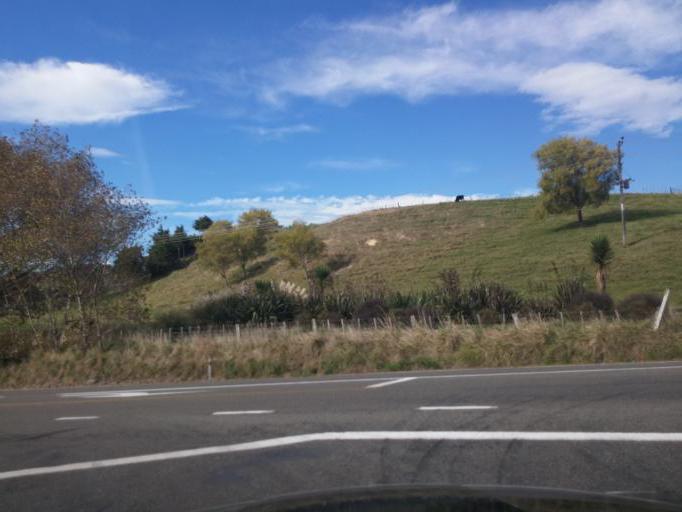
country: NZ
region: Manawatu-Wanganui
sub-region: Palmerston North City
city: Palmerston North
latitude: -40.3946
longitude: 175.6296
